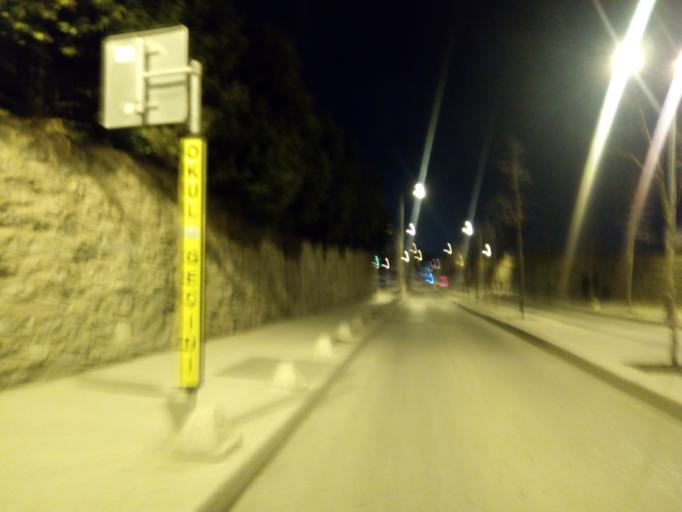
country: TR
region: Istanbul
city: Zeytinburnu
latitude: 41.0151
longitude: 28.9138
